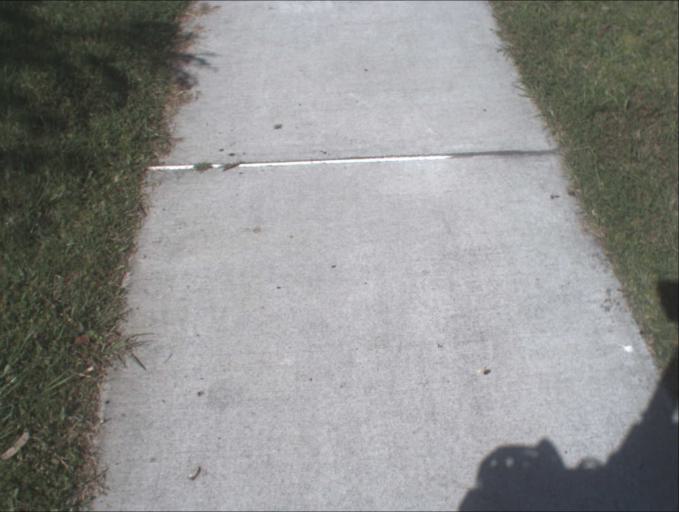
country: AU
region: Queensland
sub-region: Logan
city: Waterford West
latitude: -27.7015
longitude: 153.1602
